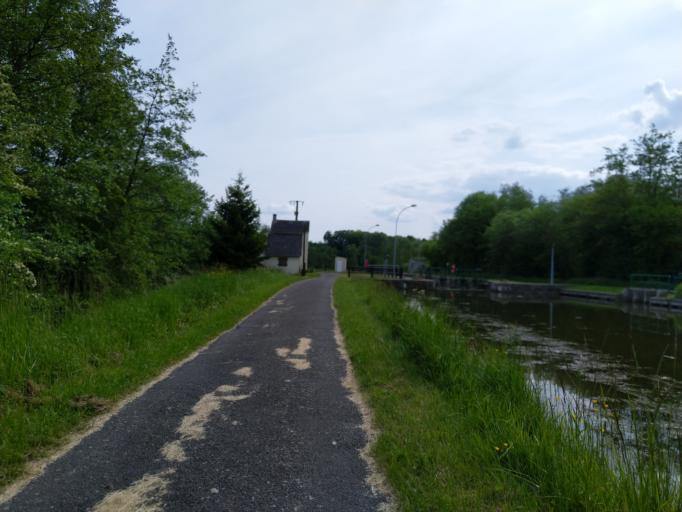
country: FR
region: Picardie
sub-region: Departement de l'Aisne
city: Etreux
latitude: 49.9614
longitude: 3.6176
